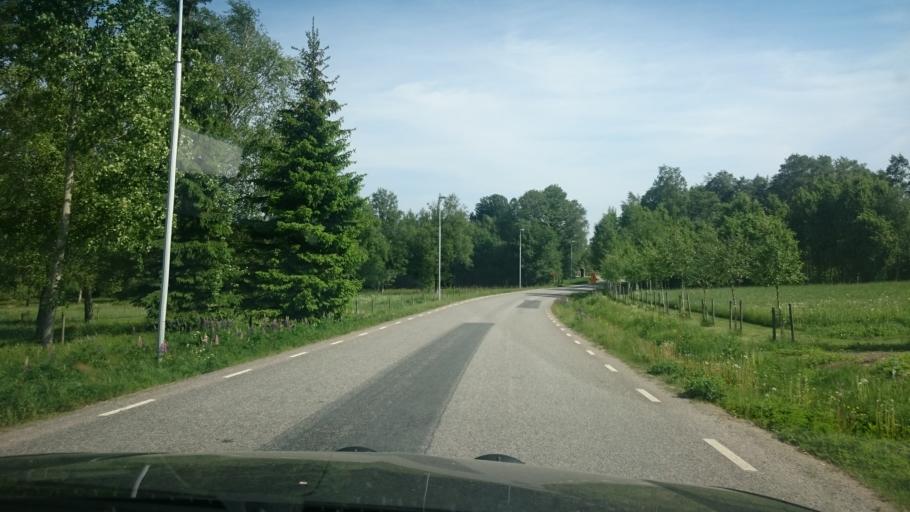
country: SE
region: Joenkoeping
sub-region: Vetlanda Kommun
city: Vetlanda
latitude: 57.2977
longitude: 15.1212
